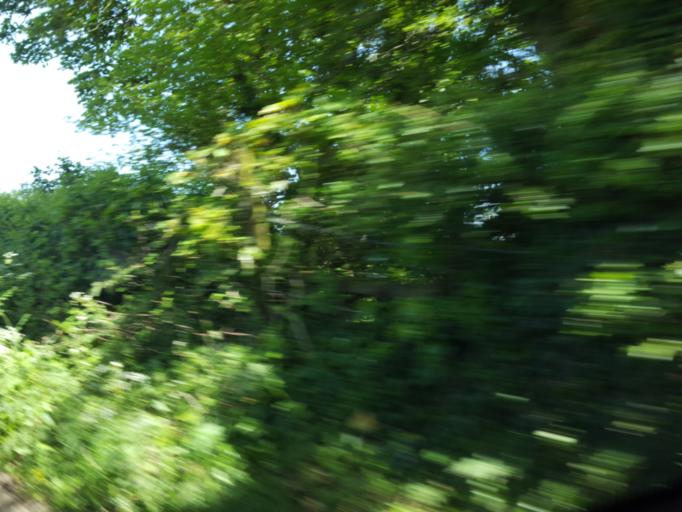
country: GB
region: England
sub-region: Gloucestershire
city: Stroud
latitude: 51.7443
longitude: -2.1787
